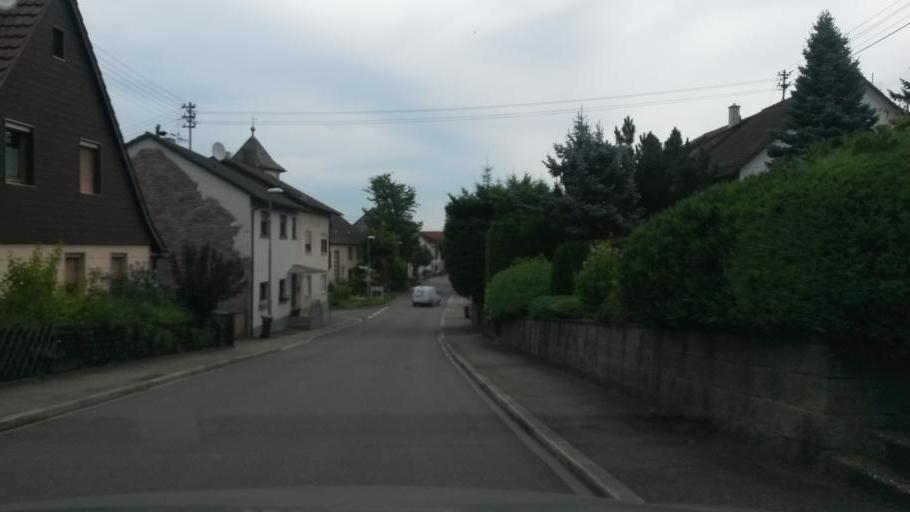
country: DE
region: Baden-Wuerttemberg
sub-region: Karlsruhe Region
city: Konigsbach-Stein
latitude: 48.9132
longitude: 8.5309
